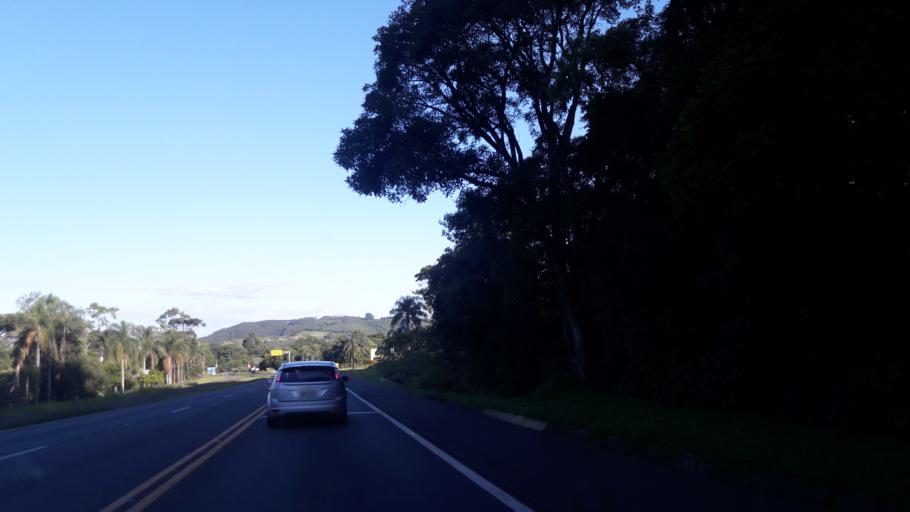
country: BR
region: Parana
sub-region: Prudentopolis
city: Prudentopolis
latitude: -25.3129
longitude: -51.1779
